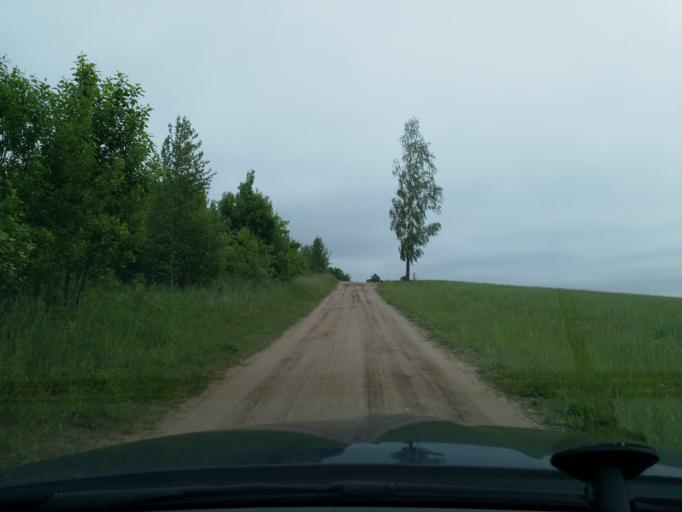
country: LV
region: Kuldigas Rajons
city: Kuldiga
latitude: 56.8795
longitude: 21.8239
